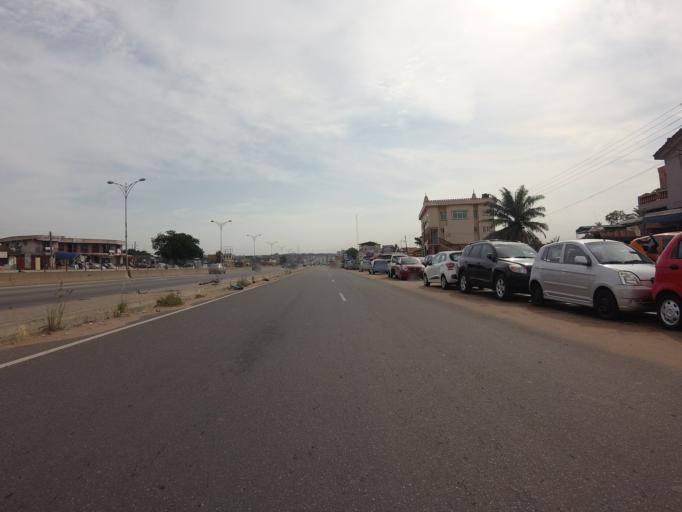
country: GH
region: Greater Accra
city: Dome
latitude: 5.6101
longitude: -0.2350
